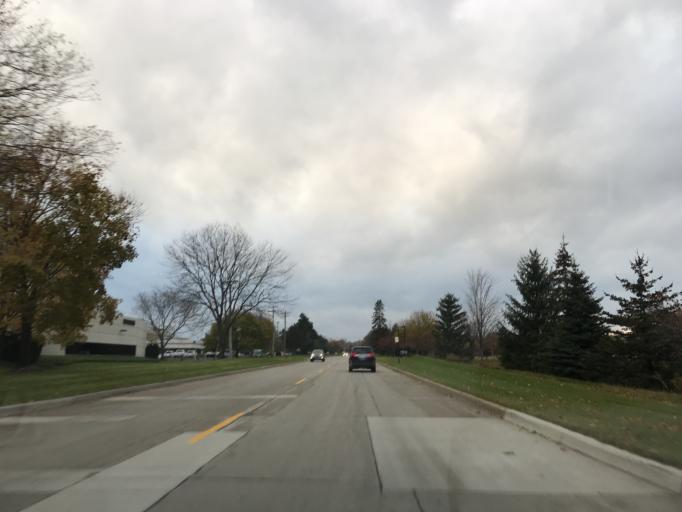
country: US
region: Michigan
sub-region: Oakland County
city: Novi
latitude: 42.4901
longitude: -83.4268
